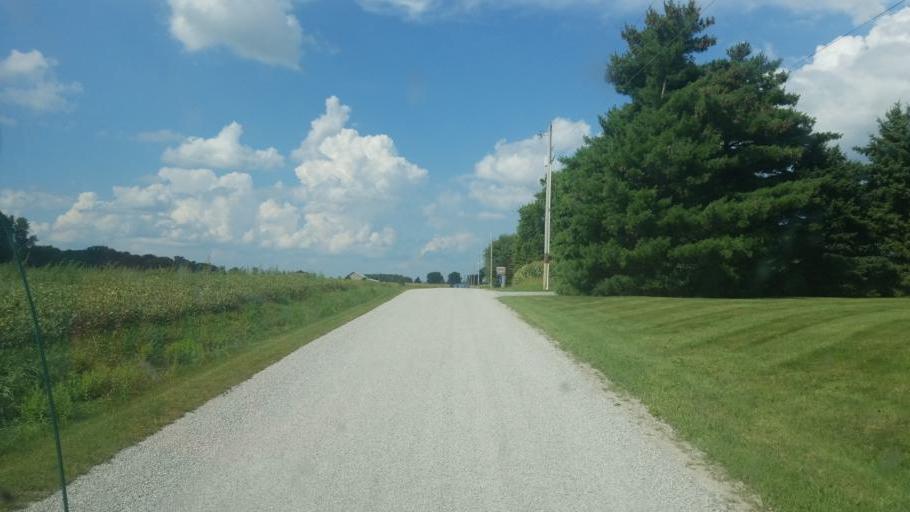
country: US
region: Ohio
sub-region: Huron County
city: Willard
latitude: 40.9852
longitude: -82.7967
